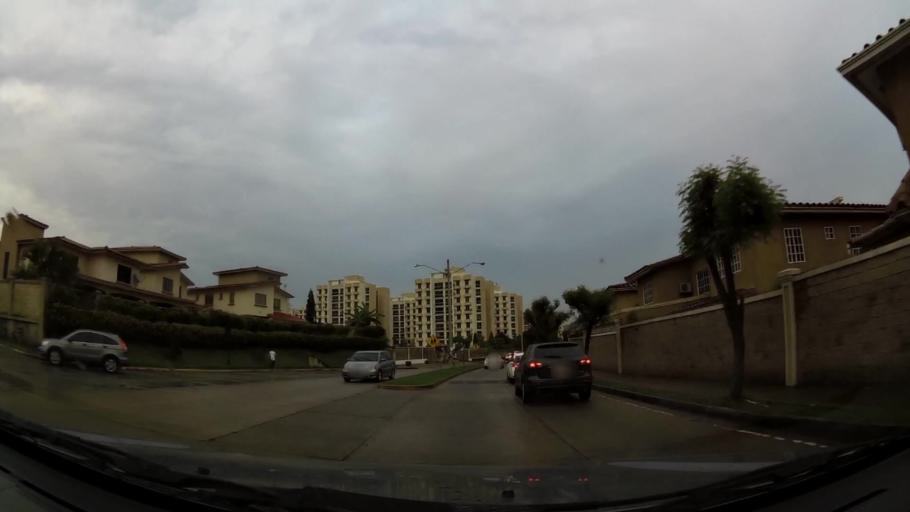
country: PA
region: Panama
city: Panama
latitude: 9.0352
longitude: -79.5321
